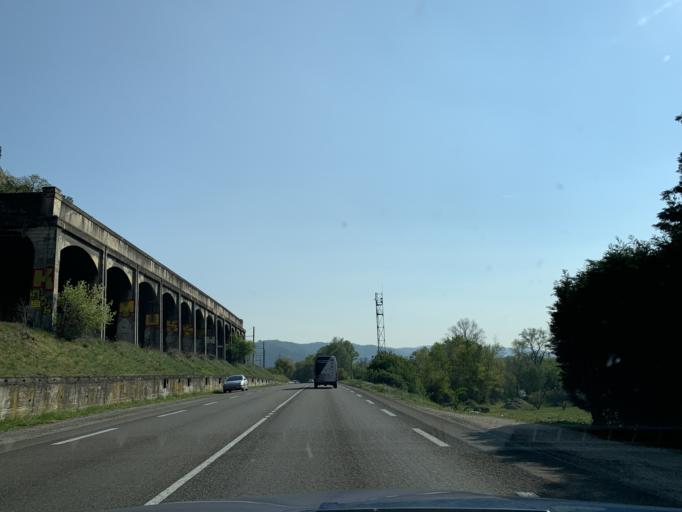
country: FR
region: Rhone-Alpes
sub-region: Departement de l'Ardeche
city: Saint-Jean-de-Muzols
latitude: 45.0925
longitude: 4.8347
